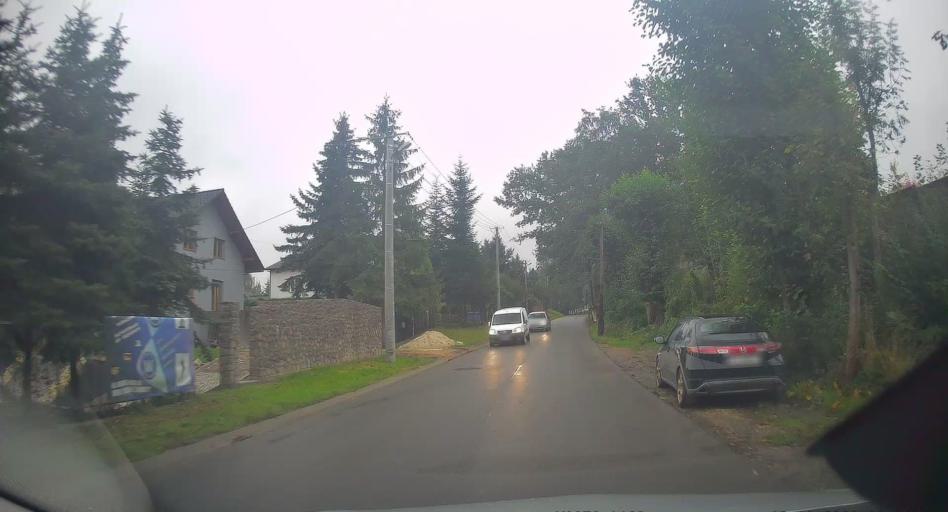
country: PL
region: Lesser Poland Voivodeship
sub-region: Powiat krakowski
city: Ochojno
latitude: 50.0100
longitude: 19.9801
